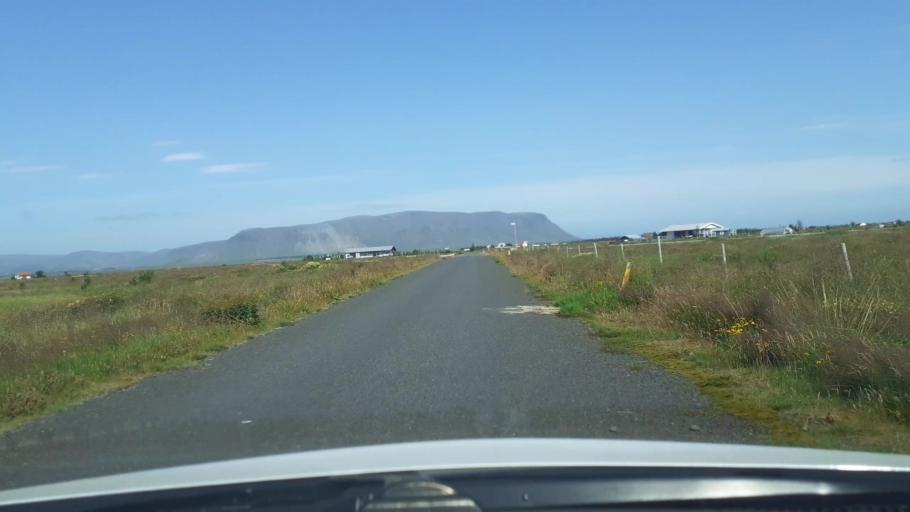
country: IS
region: South
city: Selfoss
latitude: 63.8976
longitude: -21.0824
